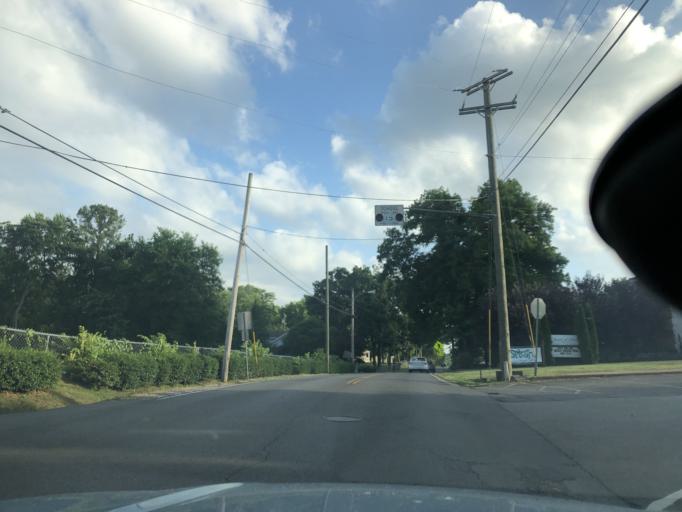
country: US
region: Tennessee
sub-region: Davidson County
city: Oak Hill
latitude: 36.1079
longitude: -86.7939
